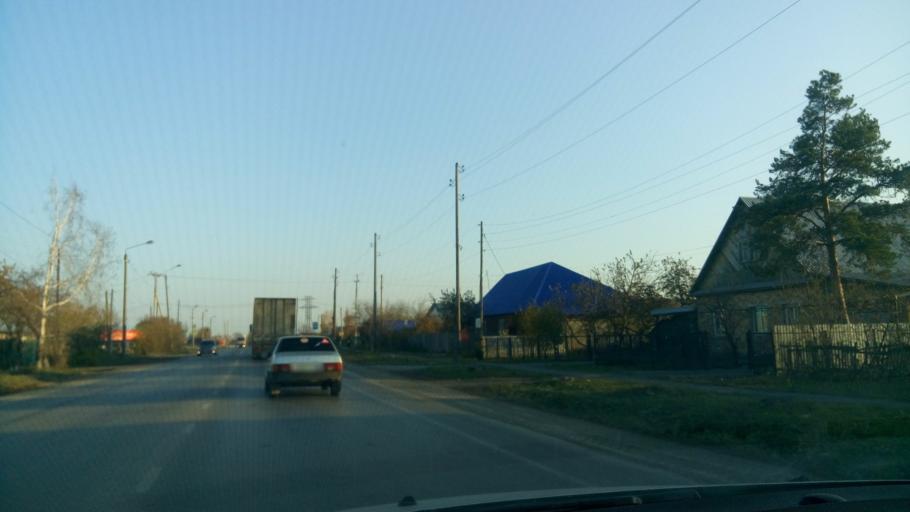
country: RU
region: Sverdlovsk
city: Bogdanovich
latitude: 56.7631
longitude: 62.0695
